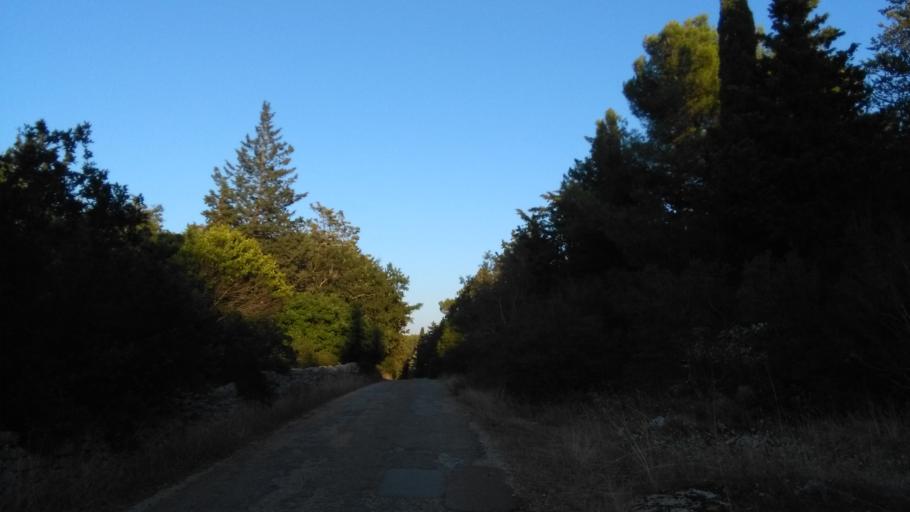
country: IT
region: Apulia
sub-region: Provincia di Bari
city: Putignano
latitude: 40.8244
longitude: 17.0822
